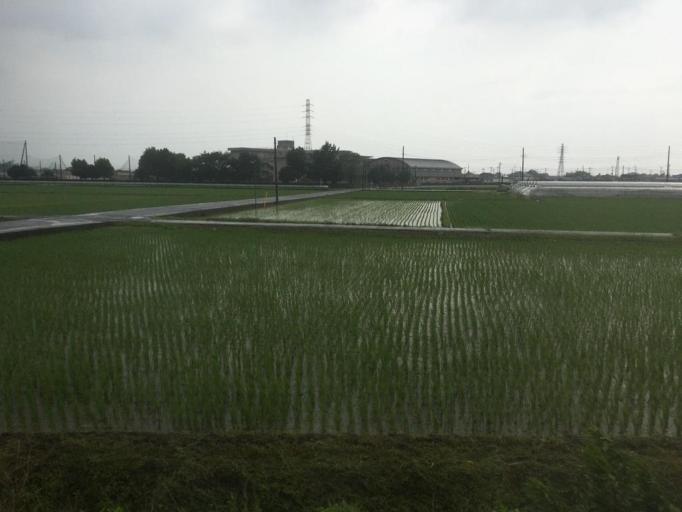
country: JP
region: Tochigi
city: Ashikaga
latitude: 36.2957
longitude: 139.4644
